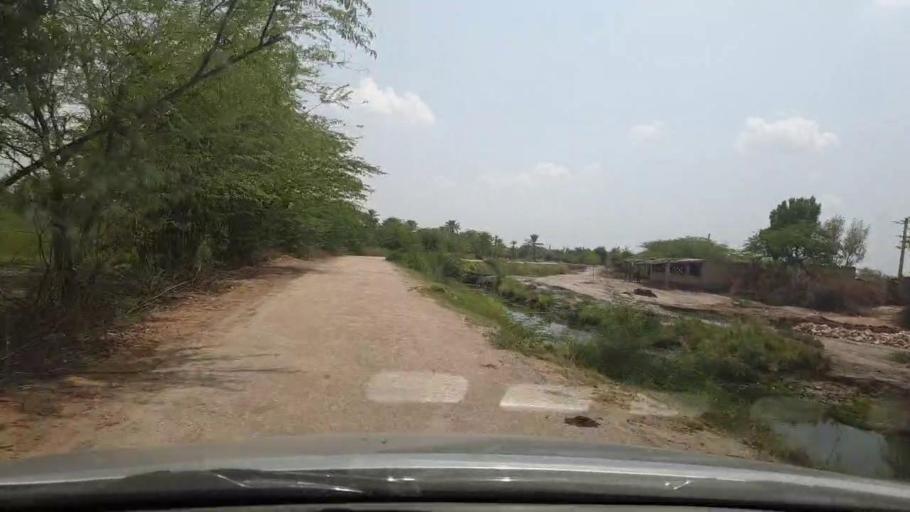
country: PK
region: Sindh
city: Kot Diji
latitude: 27.3813
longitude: 68.7136
